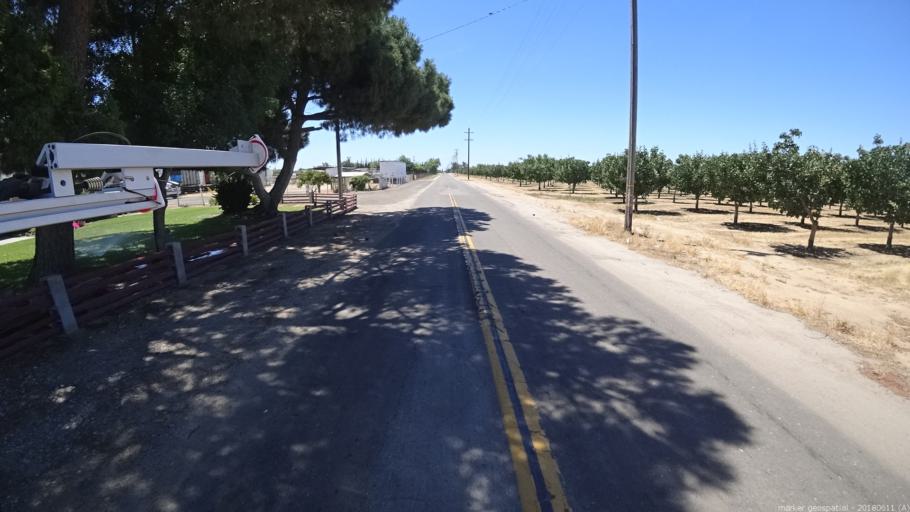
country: US
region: California
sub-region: Madera County
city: Fairmead
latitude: 37.0249
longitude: -120.1471
